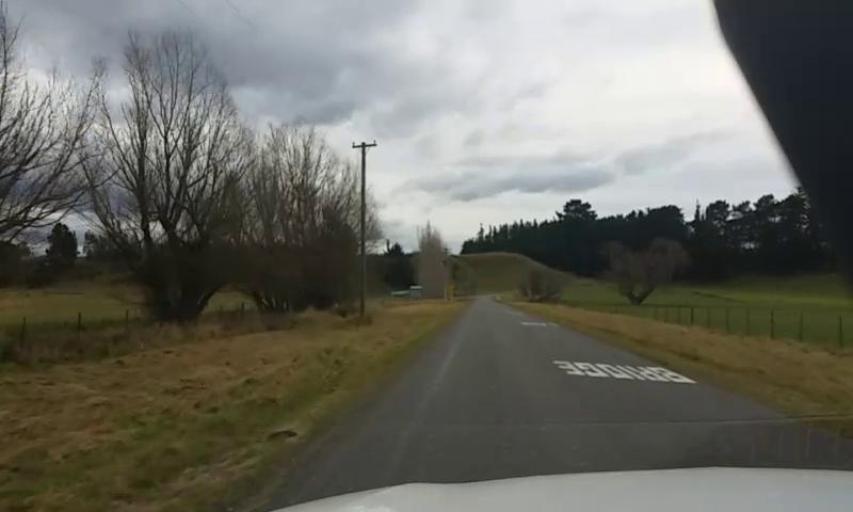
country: NZ
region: Canterbury
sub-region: Waimakariri District
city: Kaiapoi
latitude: -43.3009
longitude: 172.4378
